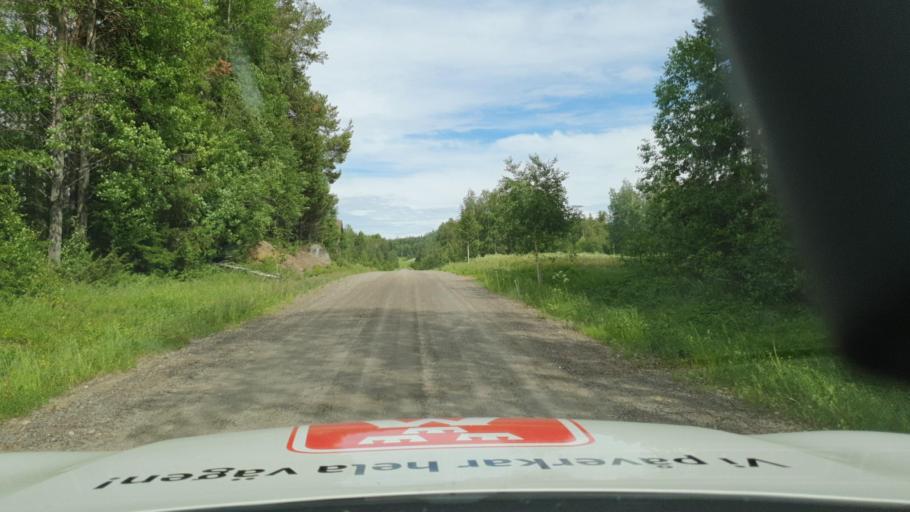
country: SE
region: Vaesterbotten
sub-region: Skelleftea Kommun
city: Burtraesk
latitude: 64.4886
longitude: 20.4872
